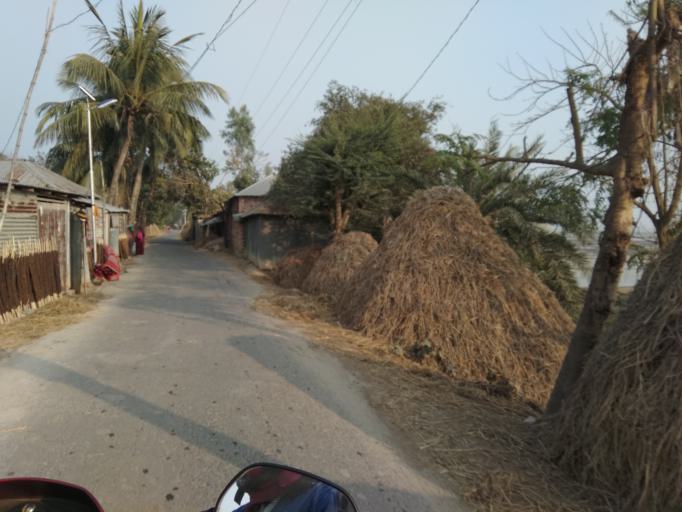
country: BD
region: Rajshahi
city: Par Naogaon
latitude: 24.4990
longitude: 89.1521
